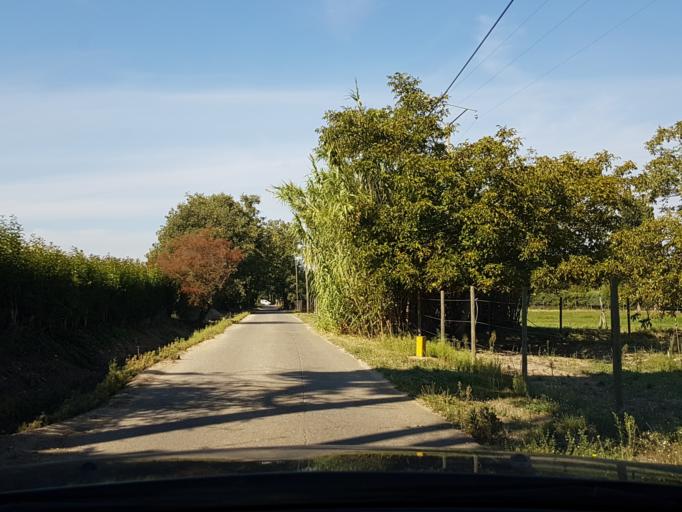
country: FR
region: Provence-Alpes-Cote d'Azur
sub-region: Departement des Bouches-du-Rhone
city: Eygalieres
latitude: 43.7748
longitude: 4.9446
